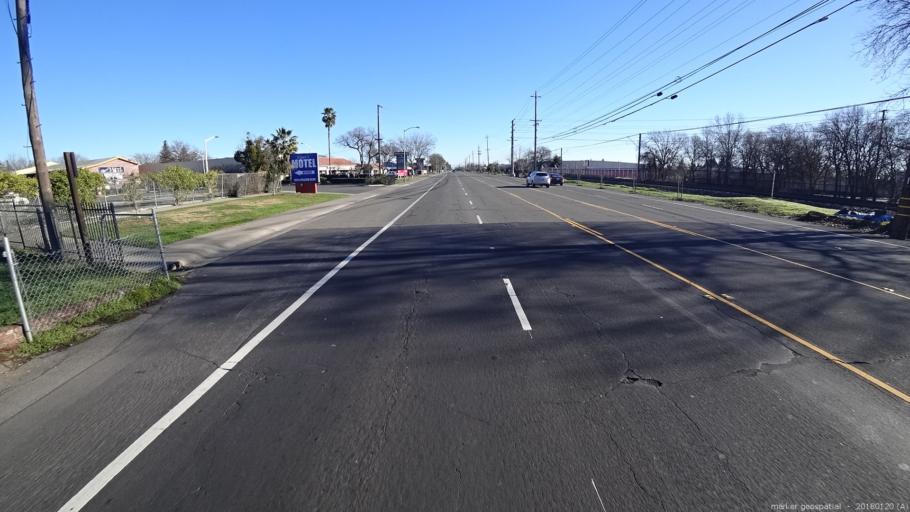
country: US
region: California
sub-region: Sacramento County
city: La Riviera
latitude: 38.5695
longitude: -121.3425
